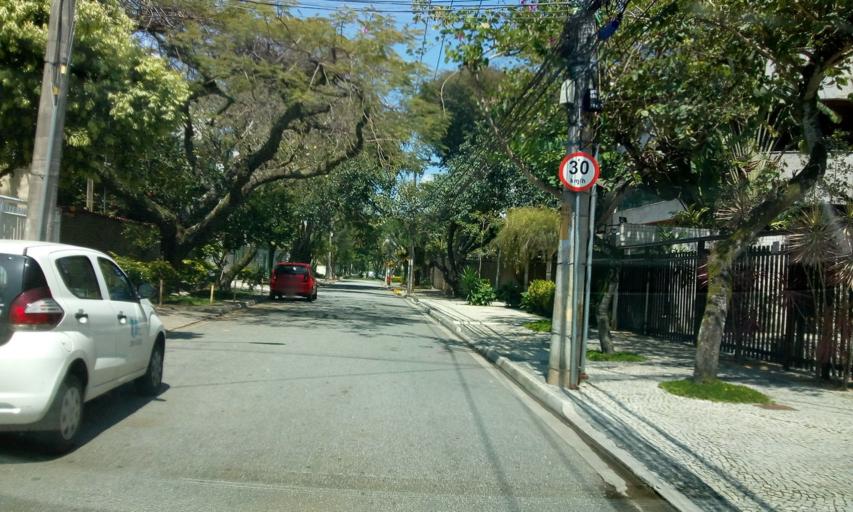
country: BR
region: Rio de Janeiro
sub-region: Nilopolis
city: Nilopolis
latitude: -23.0166
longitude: -43.4655
